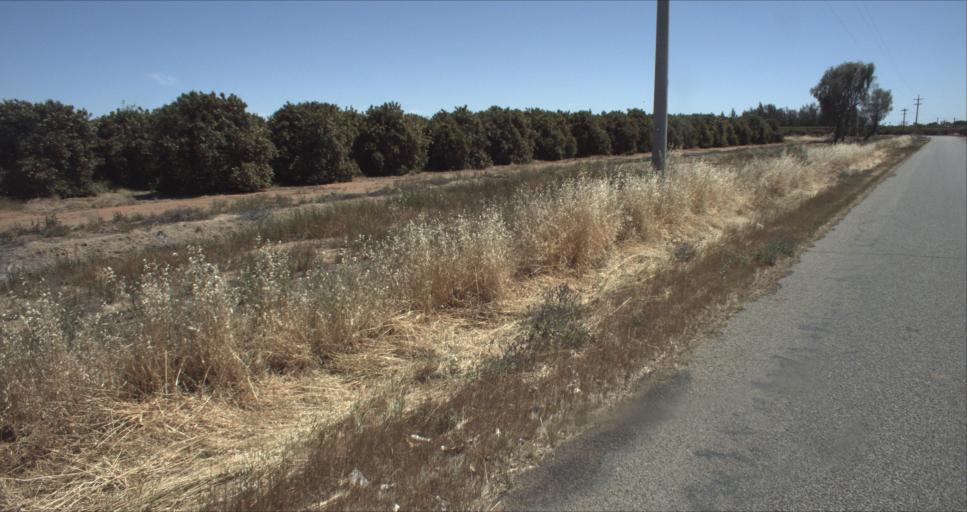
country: AU
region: New South Wales
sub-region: Leeton
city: Leeton
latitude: -34.5355
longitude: 146.3571
